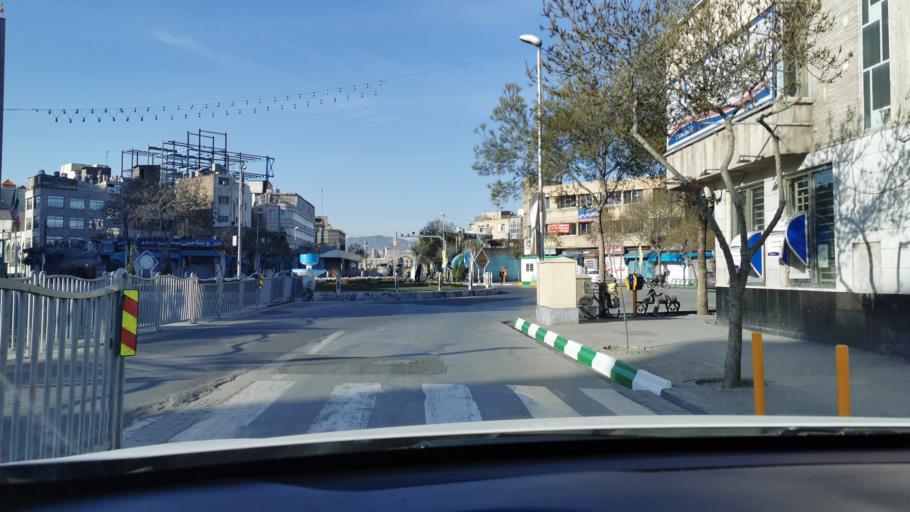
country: IR
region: Razavi Khorasan
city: Mashhad
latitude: 36.2922
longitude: 59.6223
